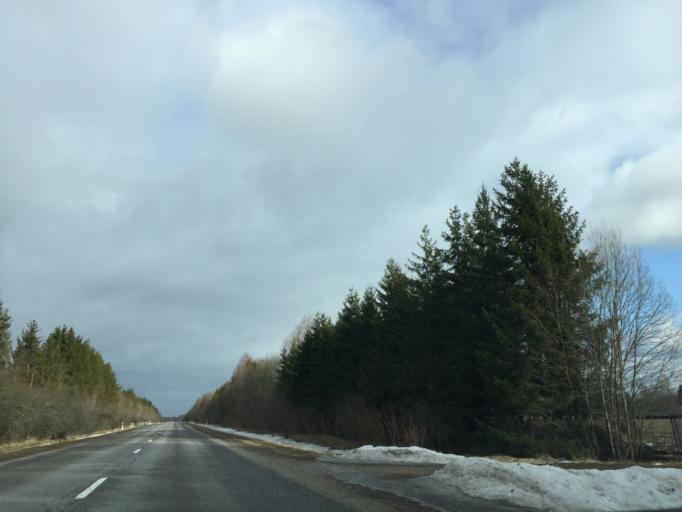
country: LV
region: Aloja
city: Staicele
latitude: 57.8881
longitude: 24.6131
